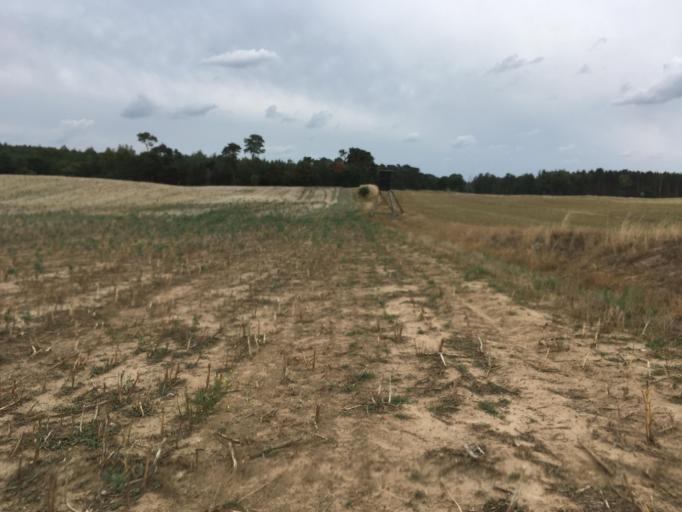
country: DE
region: Brandenburg
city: Passow
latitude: 53.1189
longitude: 14.1147
